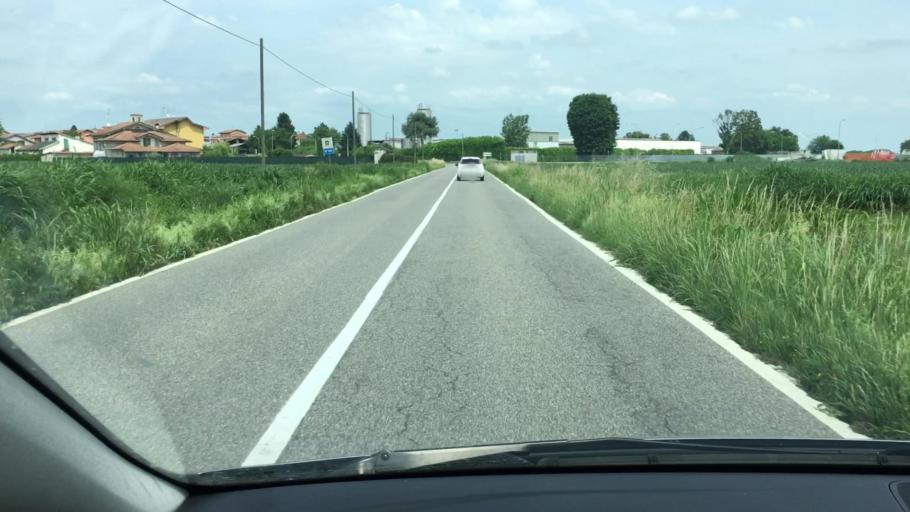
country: IT
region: Piedmont
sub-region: Provincia di Novara
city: Casalbeltrame
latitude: 45.4315
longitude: 8.4663
